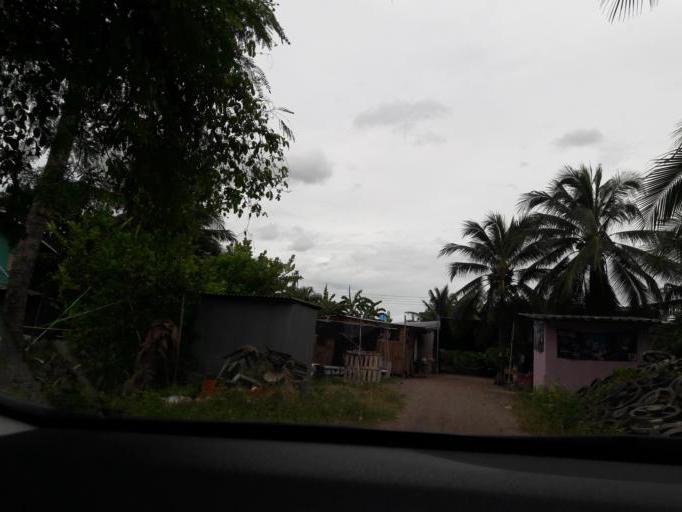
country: TH
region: Samut Sakhon
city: Ban Phaeo
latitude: 13.5411
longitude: 100.0435
